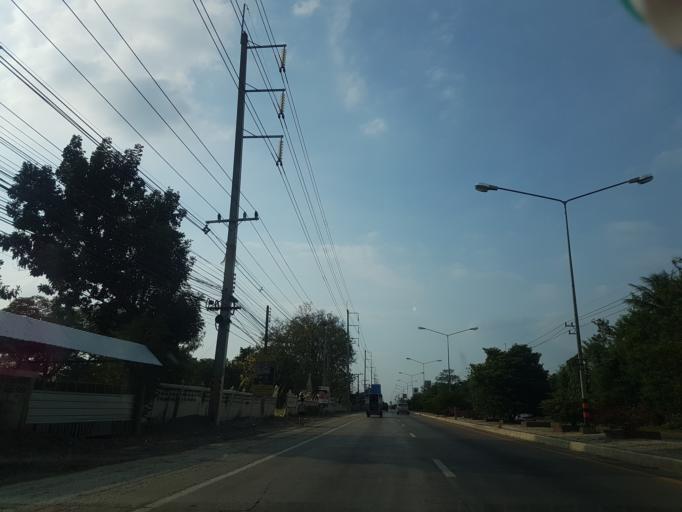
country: TH
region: Lop Buri
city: Lop Buri
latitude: 14.7656
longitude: 100.7134
